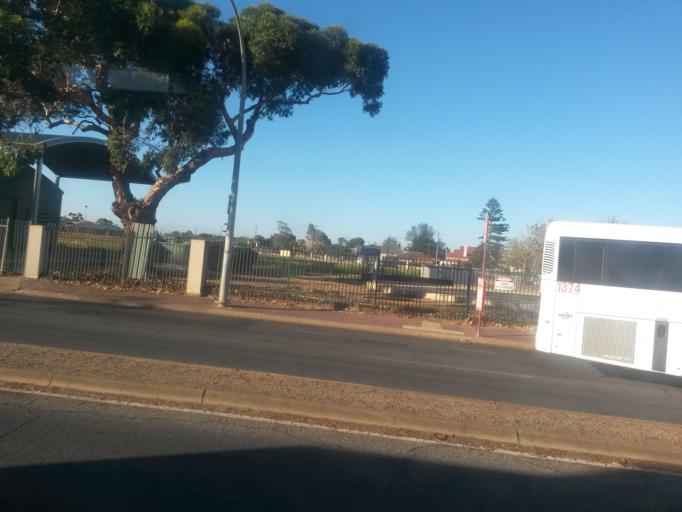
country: AU
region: South Australia
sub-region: Port Adelaide Enfield
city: Alberton
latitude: -34.8641
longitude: 138.5301
